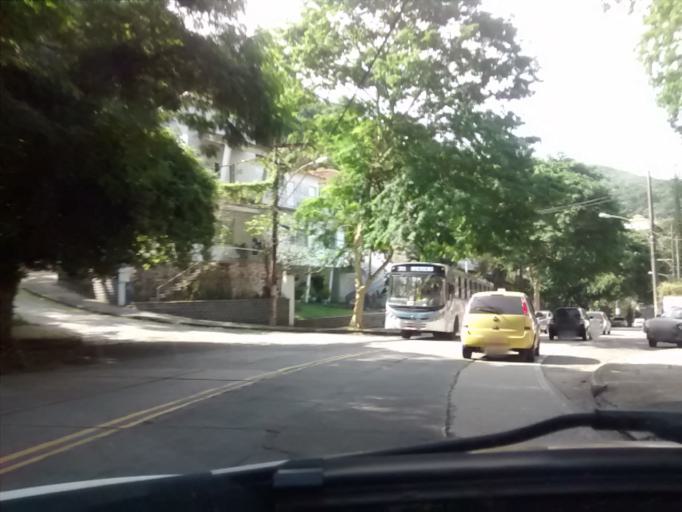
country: BR
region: Rio de Janeiro
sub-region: Rio De Janeiro
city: Rio de Janeiro
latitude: -22.9511
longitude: -43.2619
